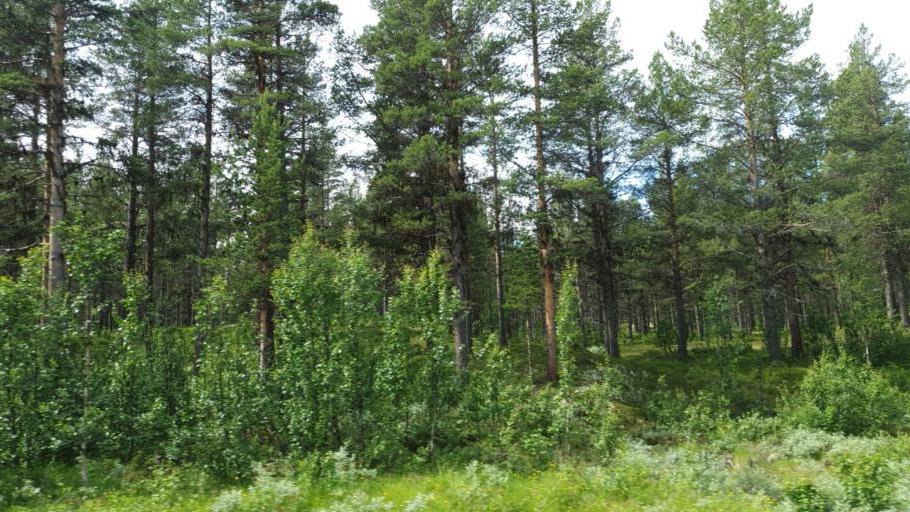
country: NO
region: Oppland
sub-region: Vaga
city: Vagamo
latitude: 61.6963
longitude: 9.0602
